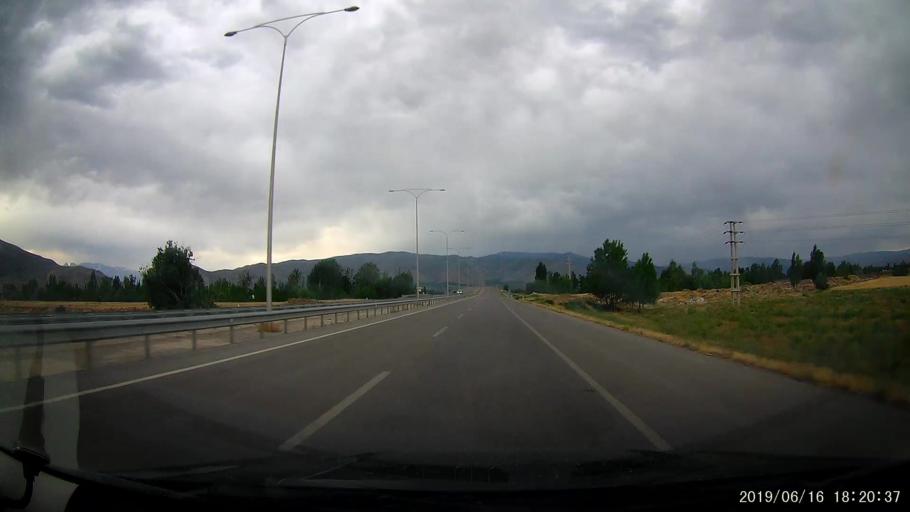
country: TR
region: Erzincan
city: Erzincan
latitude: 39.7202
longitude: 39.4649
